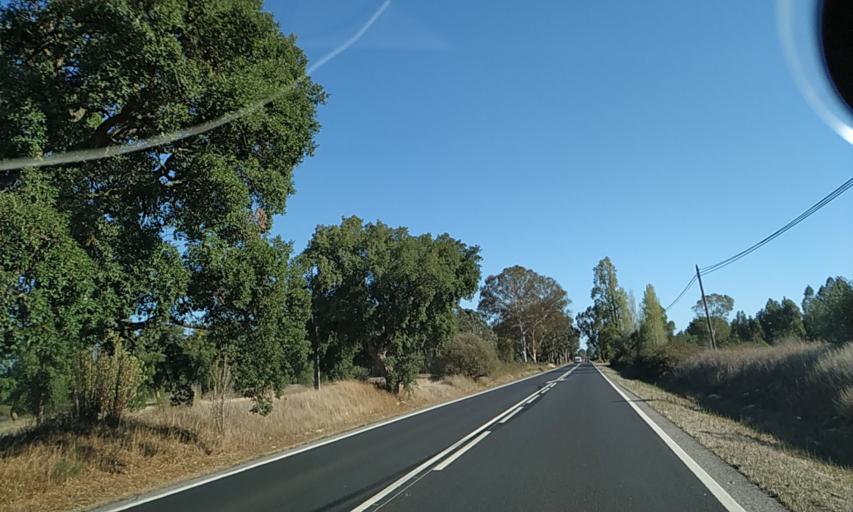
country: PT
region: Santarem
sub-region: Benavente
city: Poceirao
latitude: 38.8047
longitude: -8.8808
